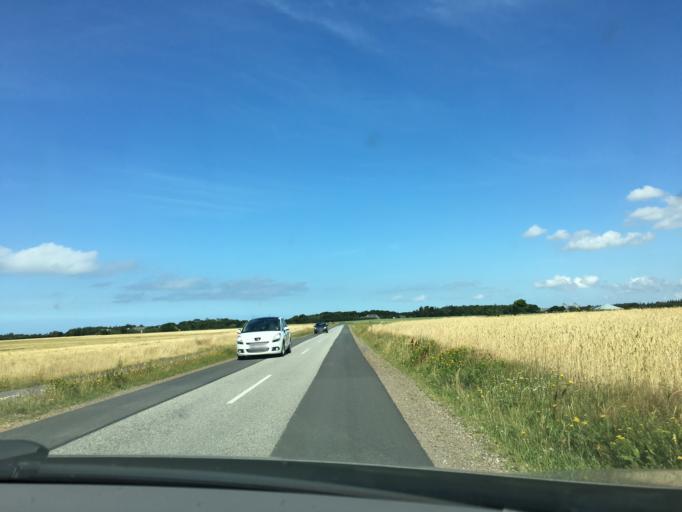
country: DK
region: Central Jutland
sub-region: Ringkobing-Skjern Kommune
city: Skjern
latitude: 55.9783
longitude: 8.3520
